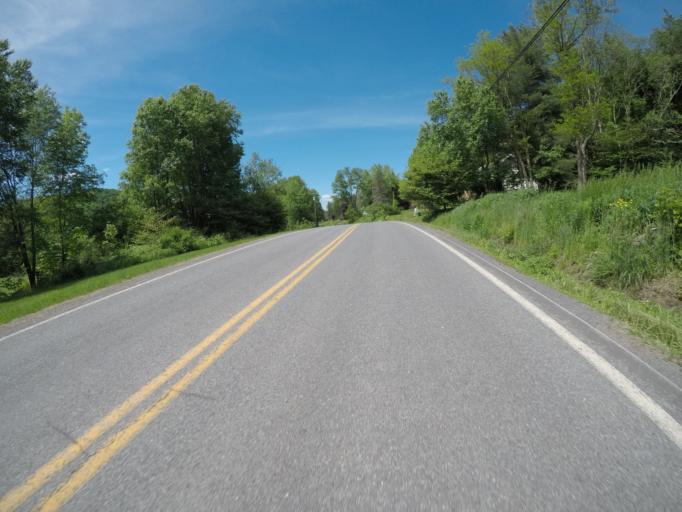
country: US
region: New York
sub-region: Delaware County
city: Delhi
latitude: 42.1445
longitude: -74.7971
